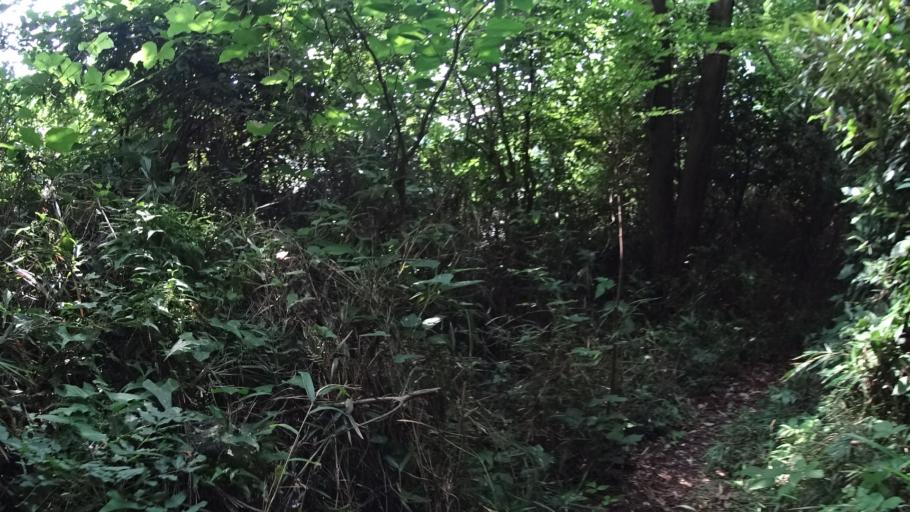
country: JP
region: Kanagawa
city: Zushi
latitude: 35.3161
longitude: 139.6041
